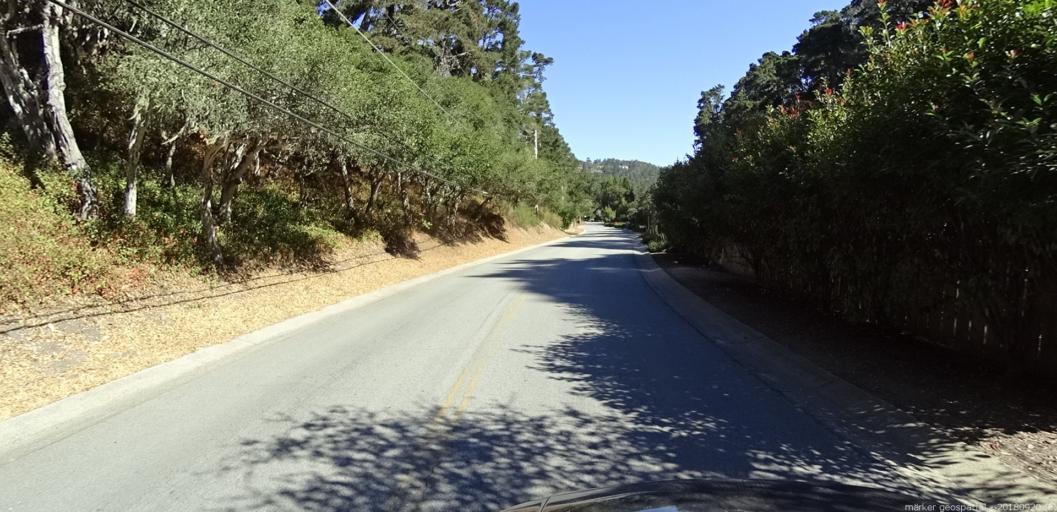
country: US
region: California
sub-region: Monterey County
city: Carmel-by-the-Sea
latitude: 36.5490
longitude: -121.8965
